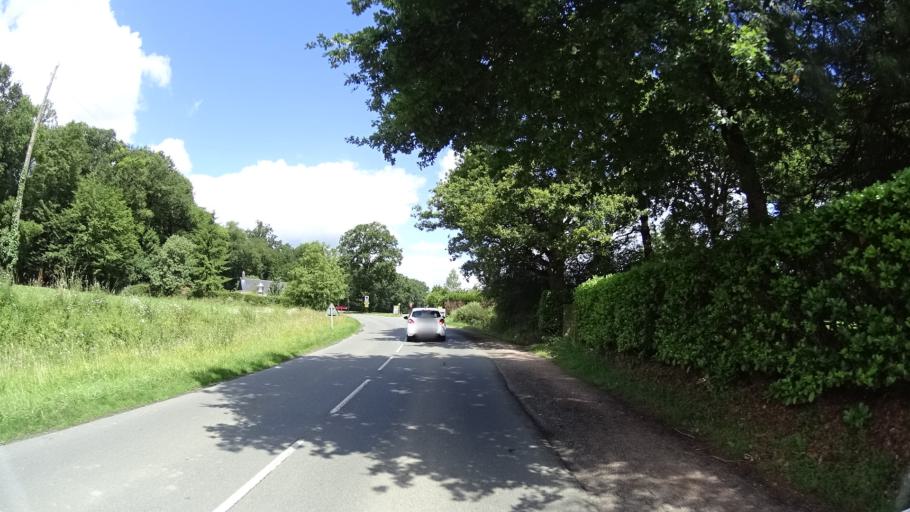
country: FR
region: Brittany
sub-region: Departement d'Ille-et-Vilaine
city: Saint-Gilles
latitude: 48.1477
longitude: -1.8299
